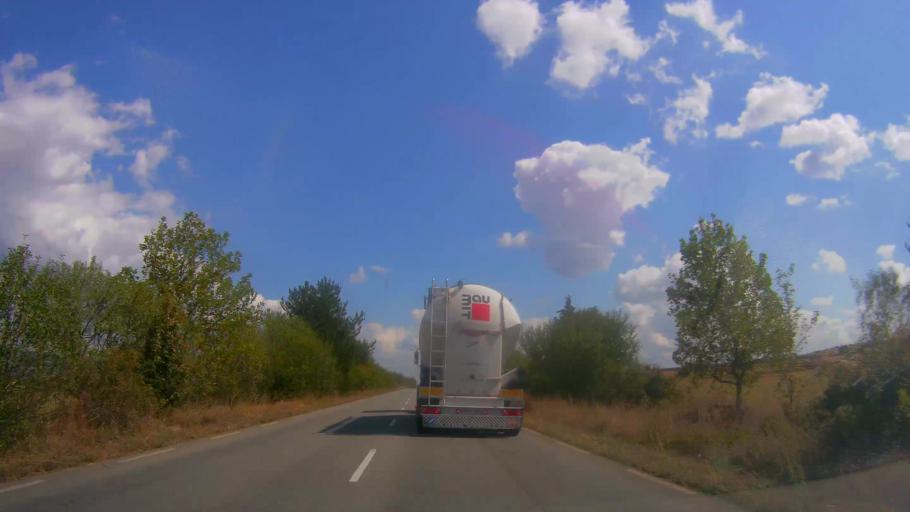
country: BG
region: Sliven
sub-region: Obshtina Tvurditsa
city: Tvurditsa
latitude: 42.6564
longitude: 25.9293
